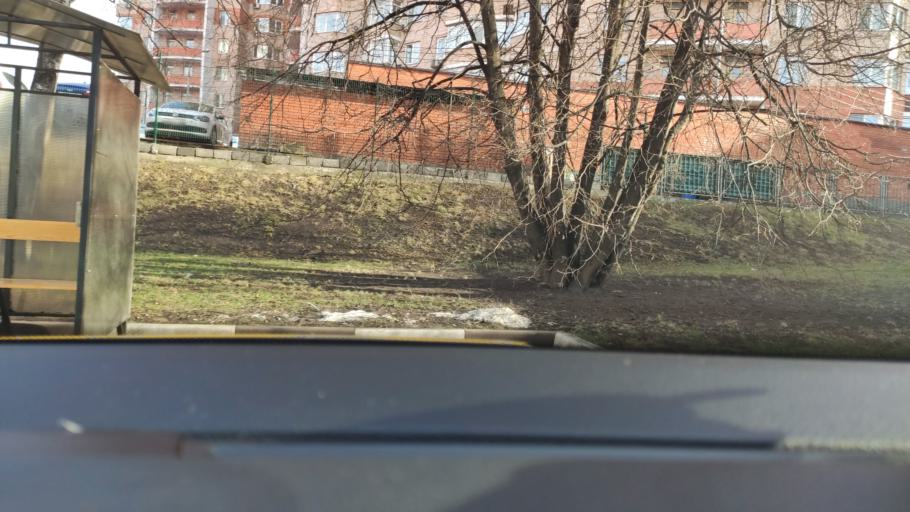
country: RU
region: Moskovskaya
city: Kozhukhovo
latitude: 55.6819
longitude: 37.6615
